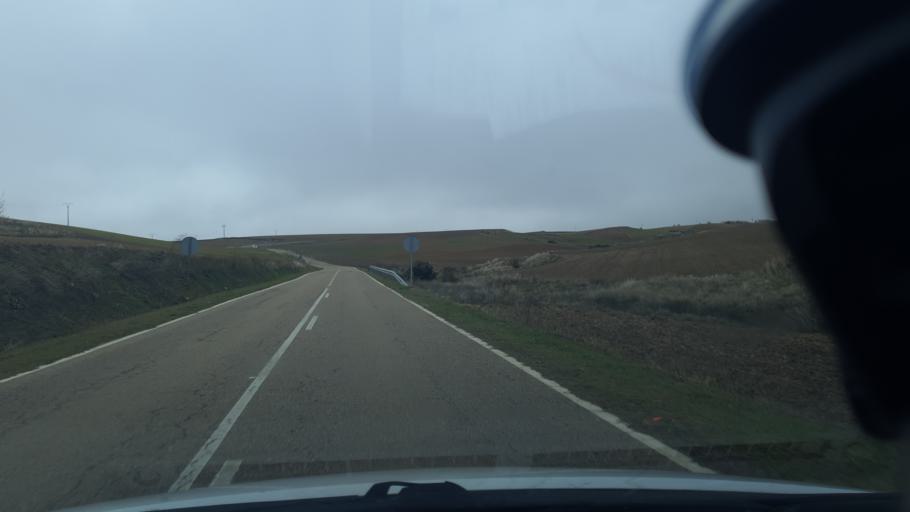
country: ES
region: Castille and Leon
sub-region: Provincia de Segovia
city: Hontanares de Eresma
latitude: 40.9878
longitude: -4.2009
